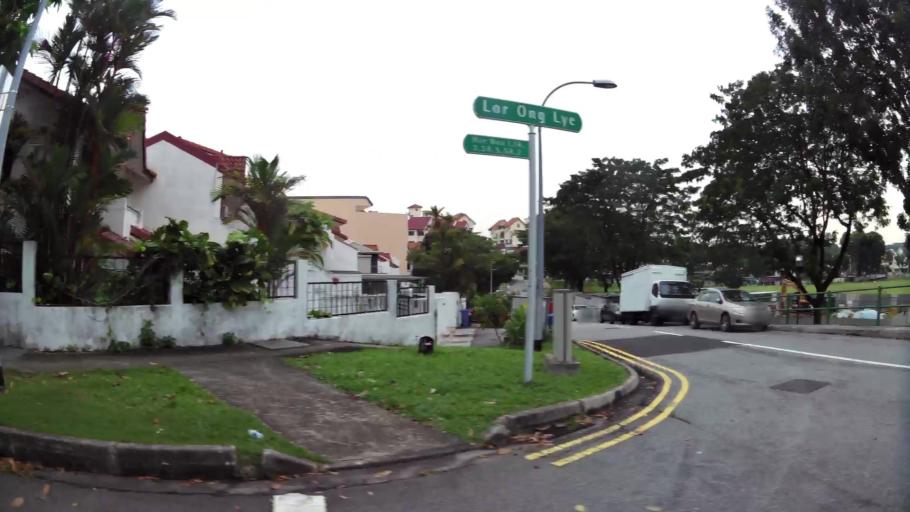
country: SG
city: Singapore
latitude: 1.3479
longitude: 103.8790
